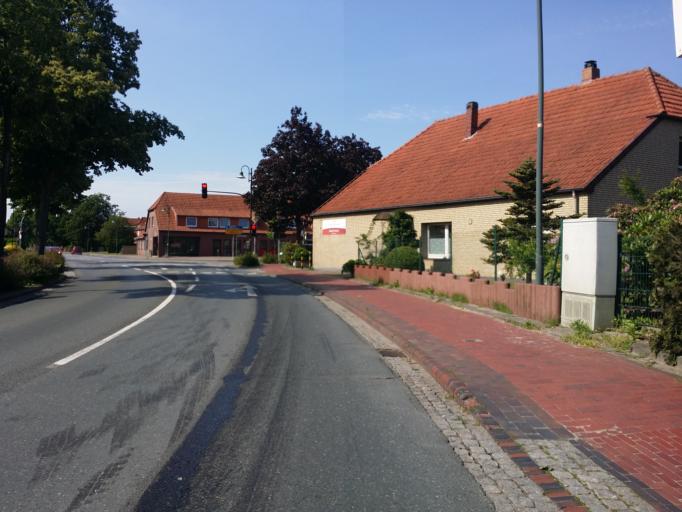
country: DE
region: Lower Saxony
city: Wiefelstede
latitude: 53.2590
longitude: 8.1156
